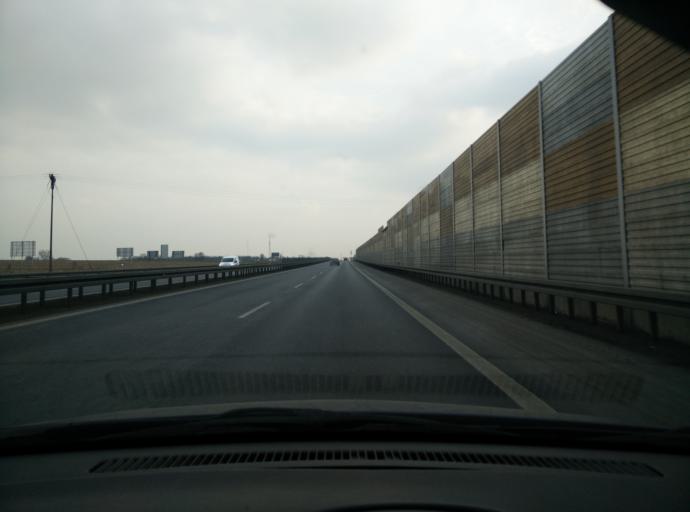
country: PL
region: Greater Poland Voivodeship
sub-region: Powiat poznanski
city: Kornik
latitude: 52.2701
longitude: 17.0672
